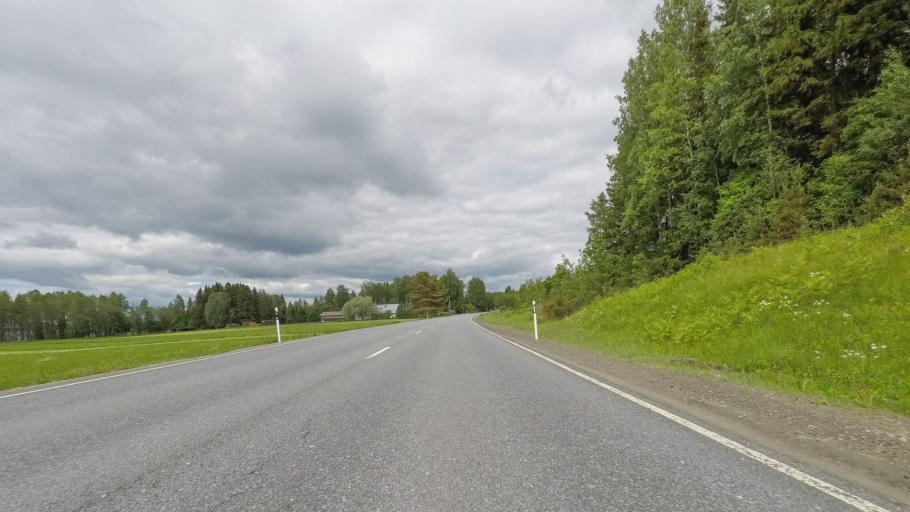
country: FI
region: Paijanne Tavastia
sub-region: Lahti
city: Hartola
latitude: 61.6266
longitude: 26.0117
